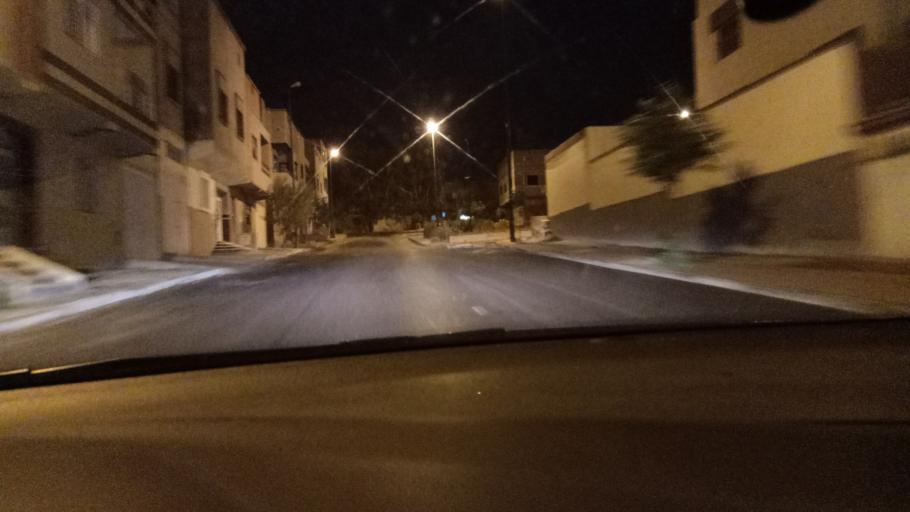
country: MA
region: Doukkala-Abda
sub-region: Safi
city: Youssoufia
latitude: 32.2415
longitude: -8.5310
